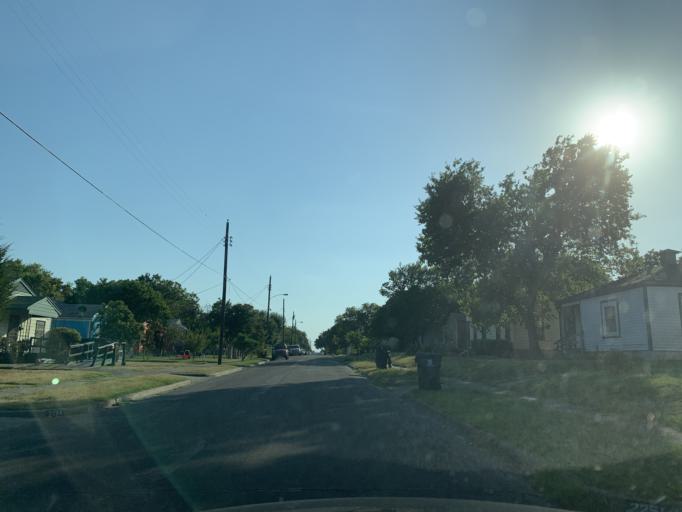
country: US
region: Texas
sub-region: Dallas County
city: Dallas
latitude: 32.7096
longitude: -96.7933
